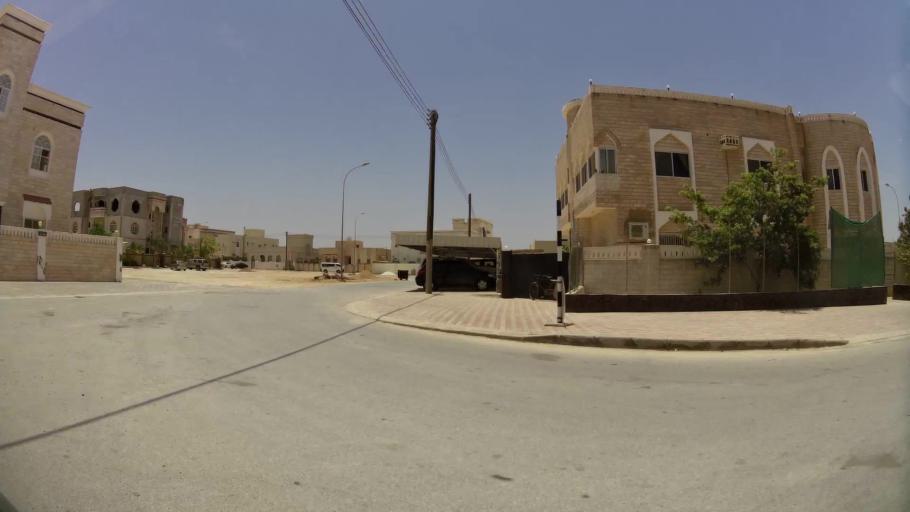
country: OM
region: Zufar
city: Salalah
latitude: 17.0814
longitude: 54.1571
